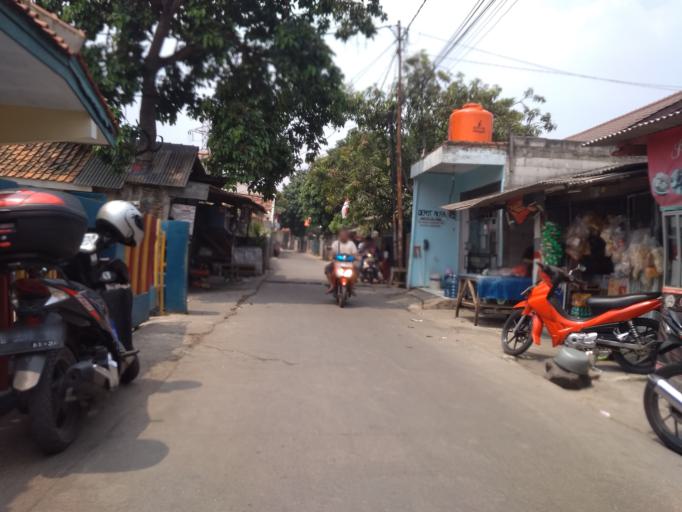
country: ID
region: West Java
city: Pamulang
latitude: -6.3231
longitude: 106.7921
